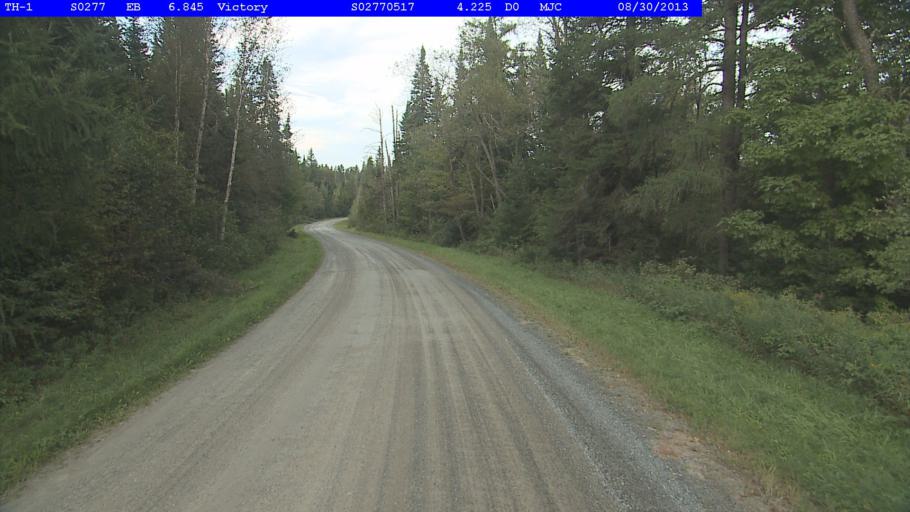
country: US
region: Vermont
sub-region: Caledonia County
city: Lyndonville
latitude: 44.5321
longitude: -71.7949
